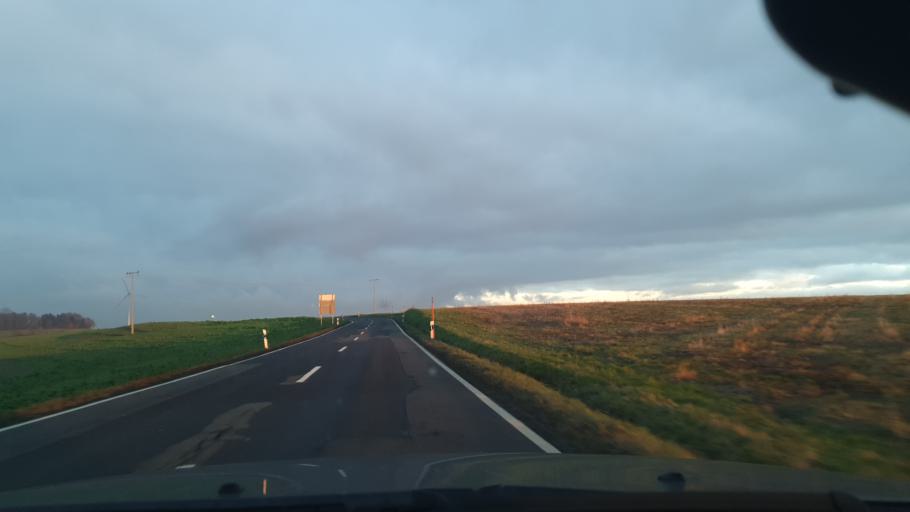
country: DE
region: Rheinland-Pfalz
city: Martinshohe
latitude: 49.3614
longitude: 7.4892
